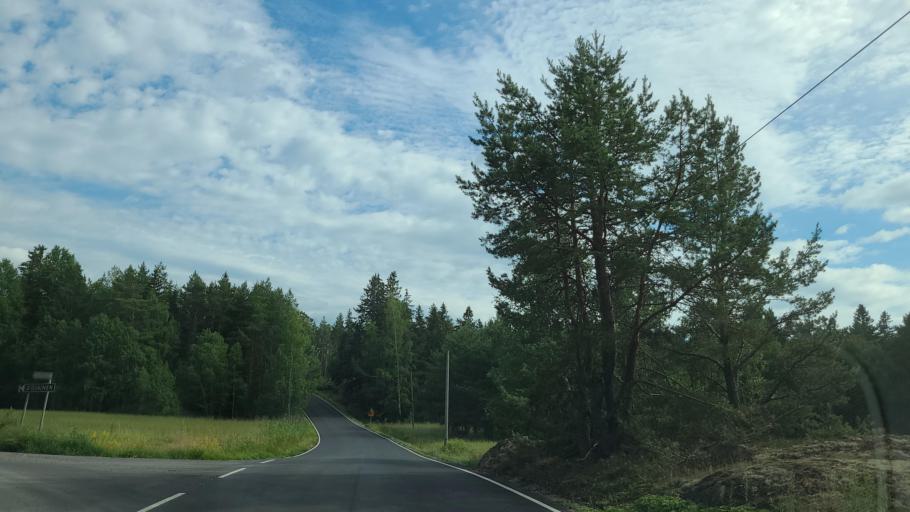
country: FI
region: Varsinais-Suomi
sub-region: Turku
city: Rymaettylae
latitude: 60.3219
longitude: 21.9560
